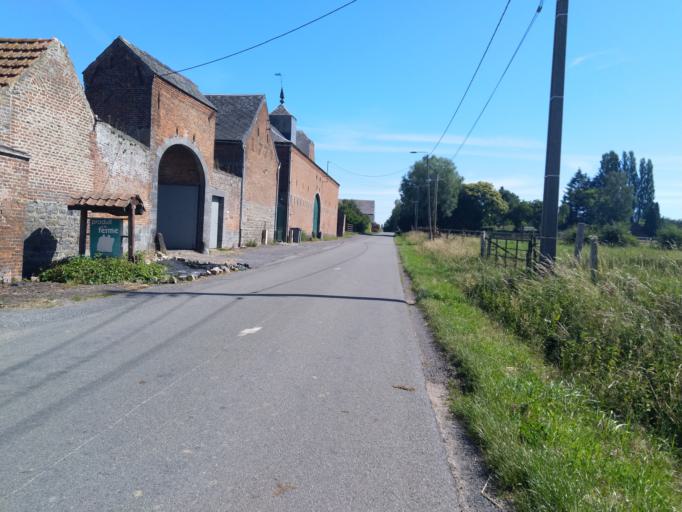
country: FR
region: Nord-Pas-de-Calais
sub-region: Departement du Nord
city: La Longueville
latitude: 50.3284
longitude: 3.8313
